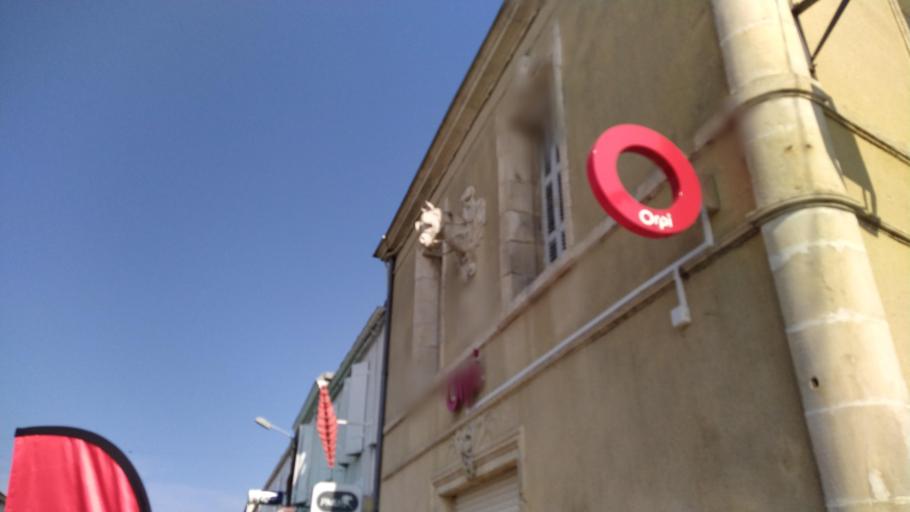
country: FR
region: Poitou-Charentes
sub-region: Departement de la Charente-Maritime
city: Saint-Trojan-les-Bains
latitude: 45.8872
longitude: -1.1970
